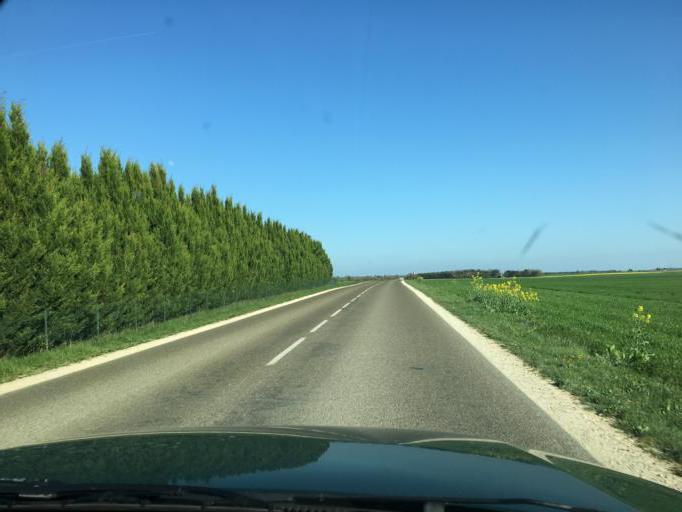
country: FR
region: Centre
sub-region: Departement du Loiret
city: Baule
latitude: 47.8523
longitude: 1.6219
